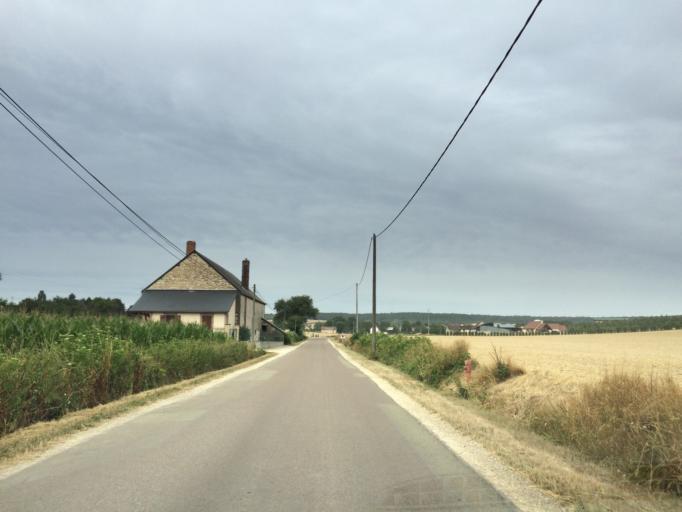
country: FR
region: Bourgogne
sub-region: Departement de l'Yonne
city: Aillant-sur-Tholon
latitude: 47.8528
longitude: 3.3425
